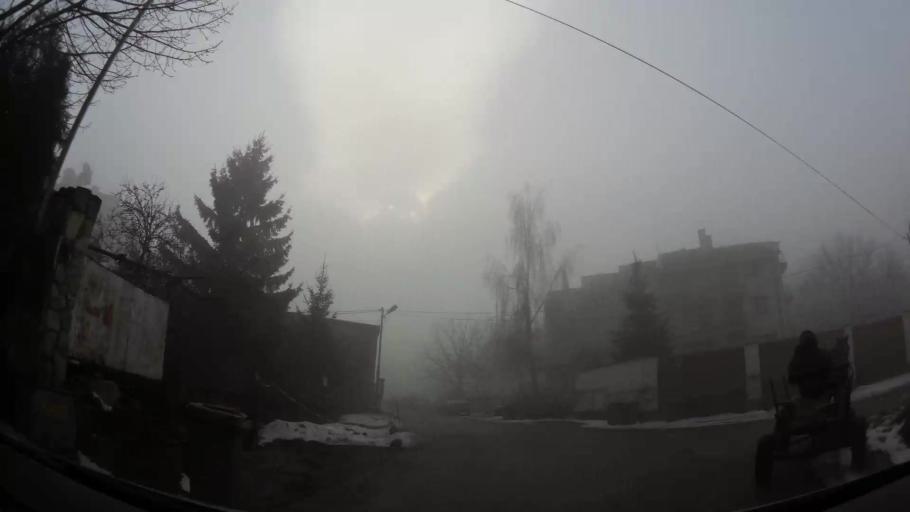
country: BG
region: Sofia-Capital
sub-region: Stolichna Obshtina
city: Sofia
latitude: 42.6537
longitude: 23.2646
